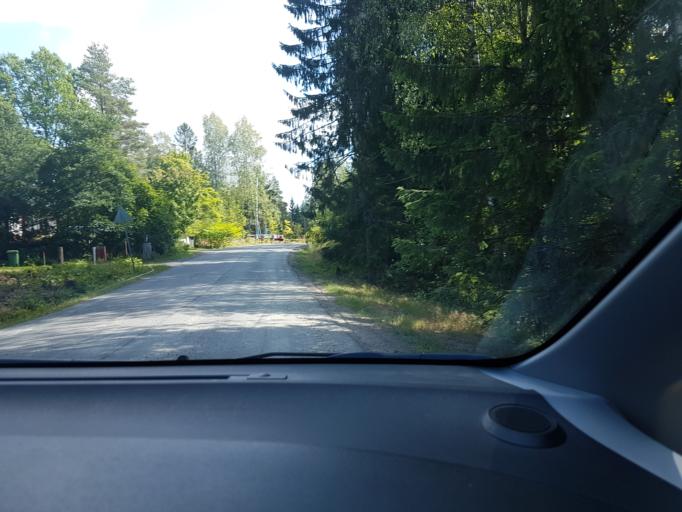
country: FI
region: Uusimaa
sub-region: Helsinki
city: Kilo
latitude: 60.3289
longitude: 24.7618
